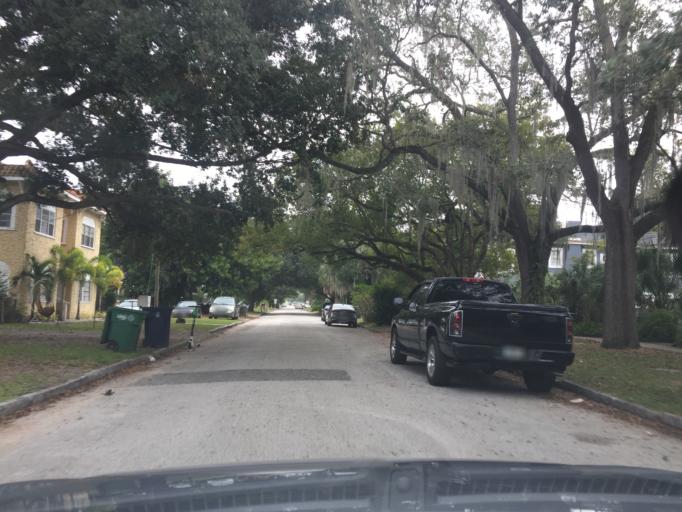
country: US
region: Florida
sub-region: Hillsborough County
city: Tampa
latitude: 27.9469
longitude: -82.4805
